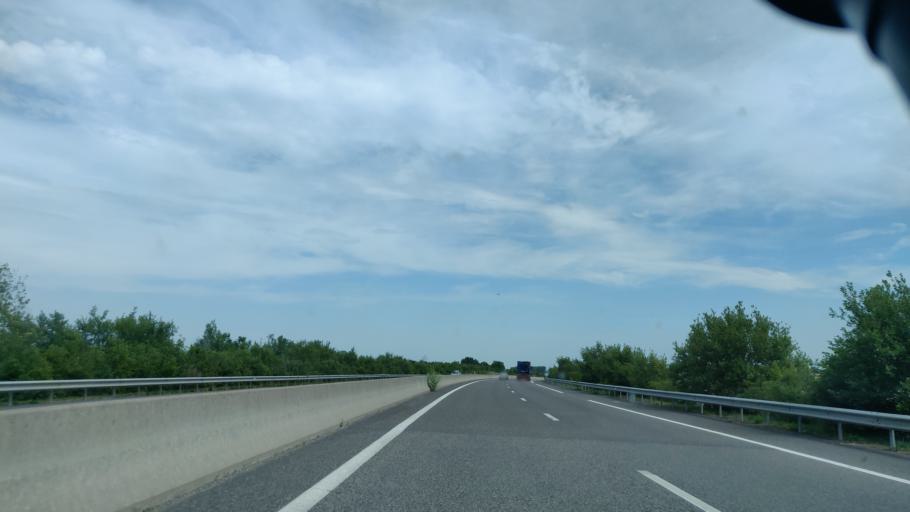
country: FR
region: Lorraine
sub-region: Departement de Meurthe-et-Moselle
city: Gerbeviller
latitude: 48.5297
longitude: 6.5917
